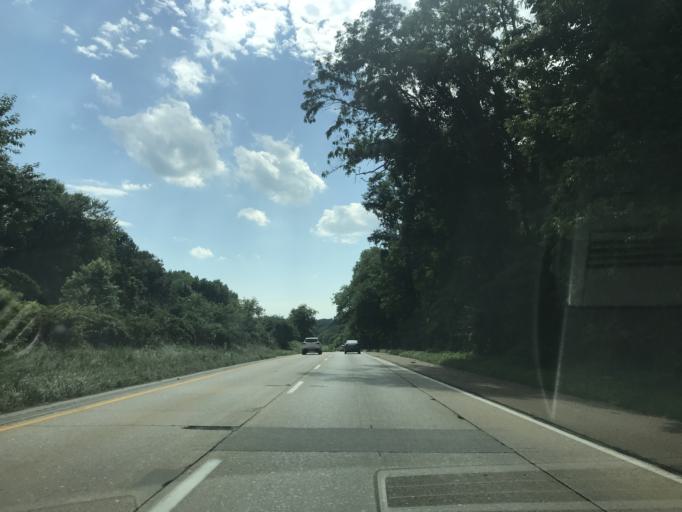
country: US
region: Pennsylvania
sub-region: Chester County
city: Kennett Square
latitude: 39.8559
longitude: -75.7211
